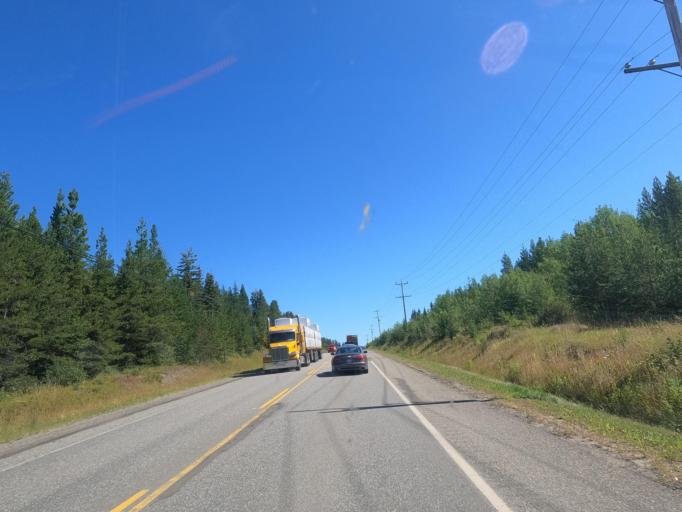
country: CA
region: British Columbia
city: Quesnel
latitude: 53.0693
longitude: -122.4297
